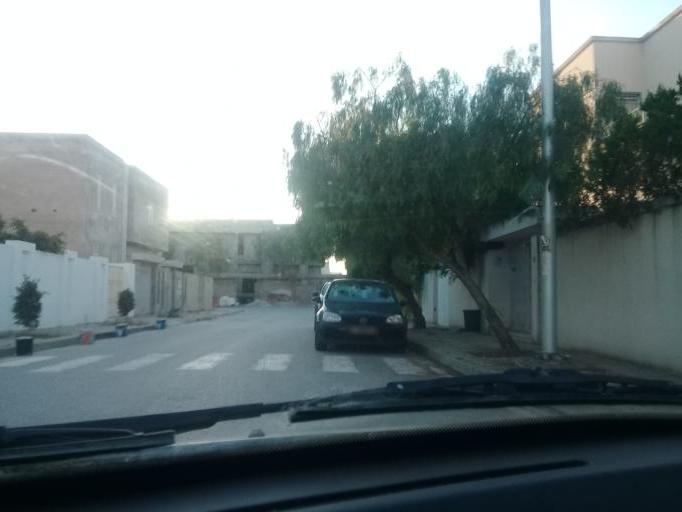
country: TN
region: Tunis
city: La Goulette
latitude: 36.8457
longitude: 10.2643
